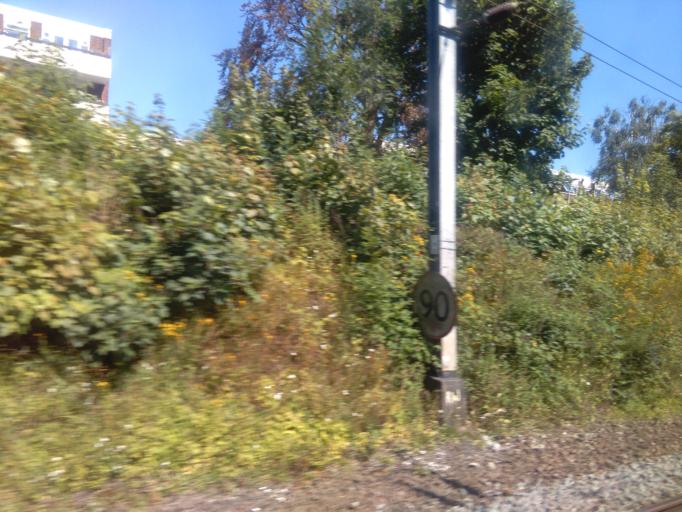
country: GB
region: England
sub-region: Hertfordshire
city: Harpenden
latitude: 51.8170
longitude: -0.3531
